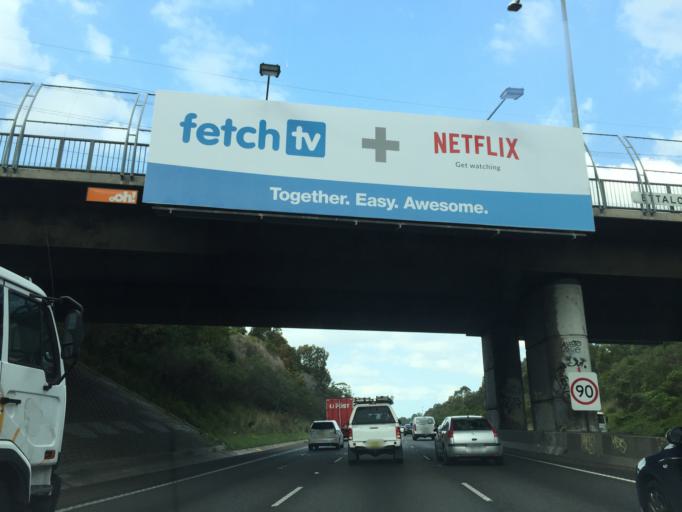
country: AU
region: New South Wales
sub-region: Holroyd
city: Girraween
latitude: -33.8131
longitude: 150.9515
